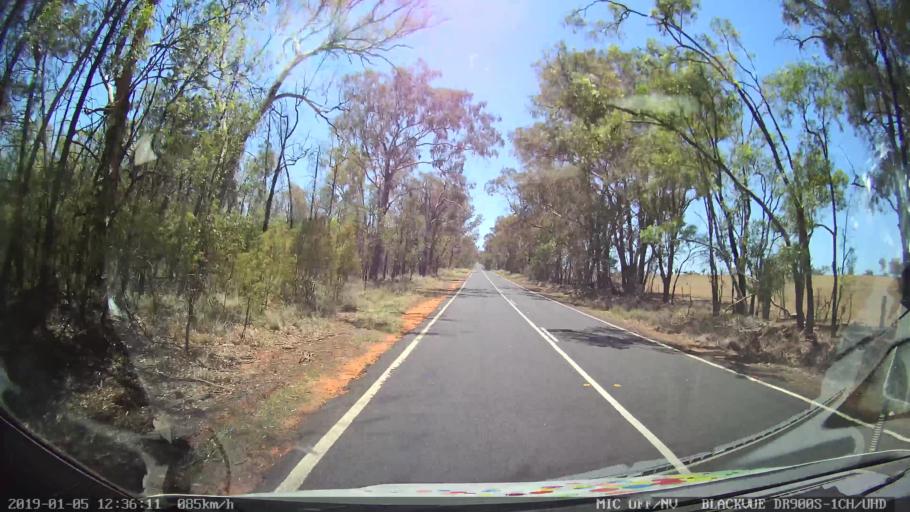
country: AU
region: New South Wales
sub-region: Warrumbungle Shire
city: Coonabarabran
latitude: -31.2078
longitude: 149.4365
